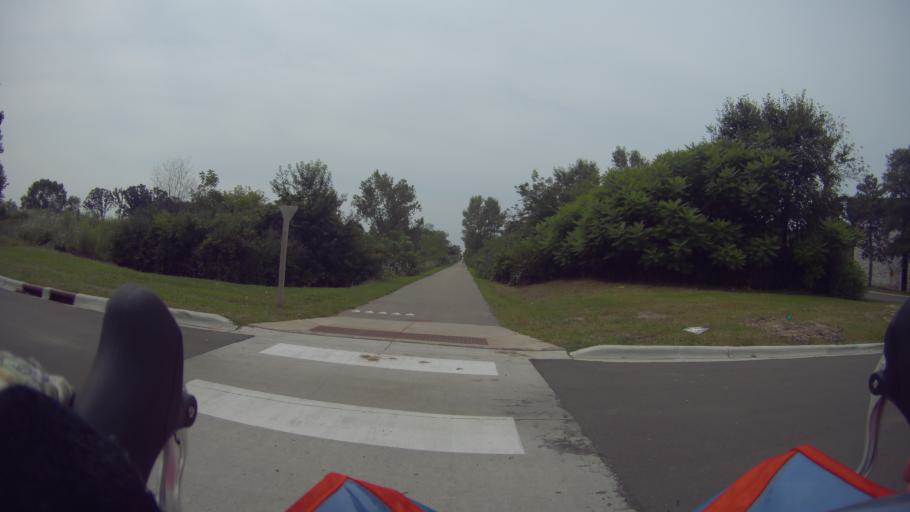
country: US
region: Wisconsin
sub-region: Dane County
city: Shorewood Hills
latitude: 43.0217
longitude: -89.4647
